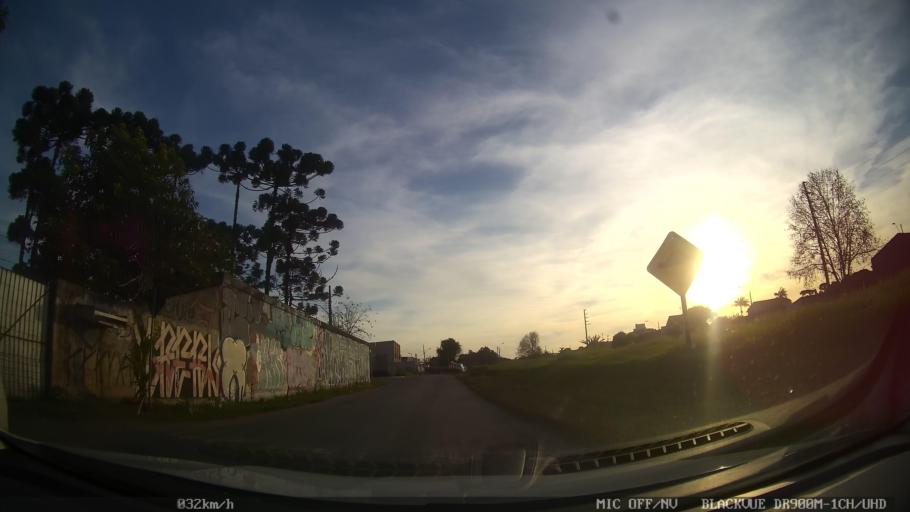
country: BR
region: Parana
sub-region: Pinhais
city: Pinhais
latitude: -25.4396
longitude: -49.1735
